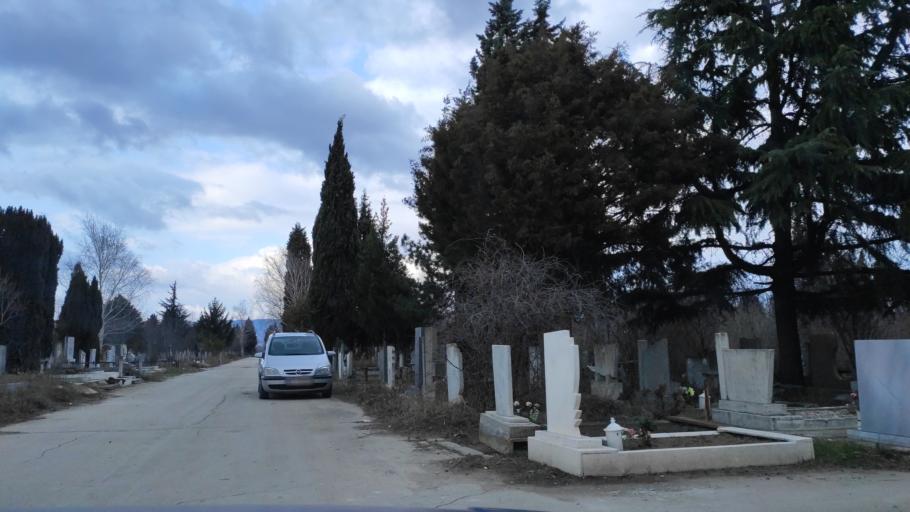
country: BG
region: Varna
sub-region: Obshtina Aksakovo
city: Aksakovo
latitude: 43.2204
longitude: 27.8090
